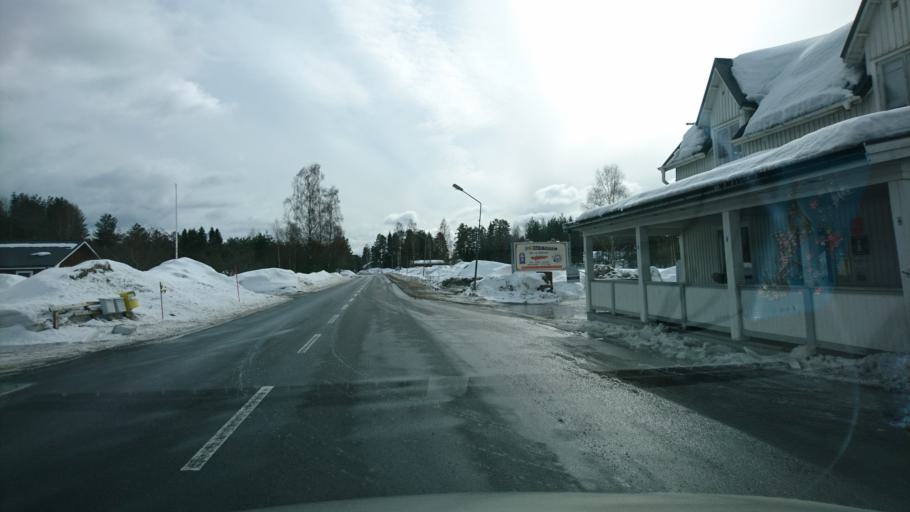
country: SE
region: Vaesternorrland
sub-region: Timra Kommun
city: Bergeforsen
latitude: 62.7790
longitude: 17.4218
